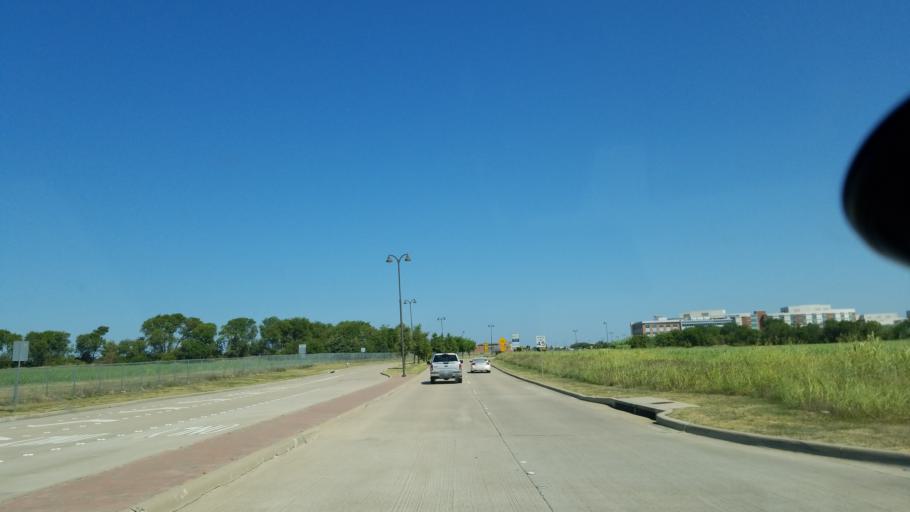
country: US
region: Texas
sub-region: Tarrant County
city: Mansfield
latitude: 32.5616
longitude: -97.0942
